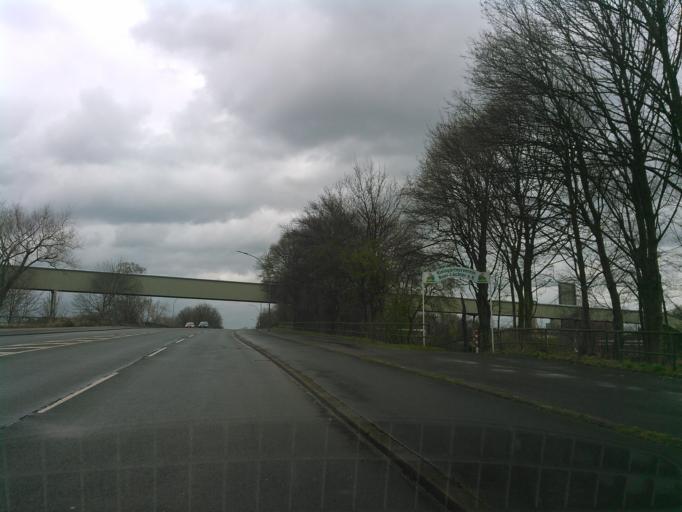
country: DE
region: North Rhine-Westphalia
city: Marl
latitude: 51.5976
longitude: 7.0667
